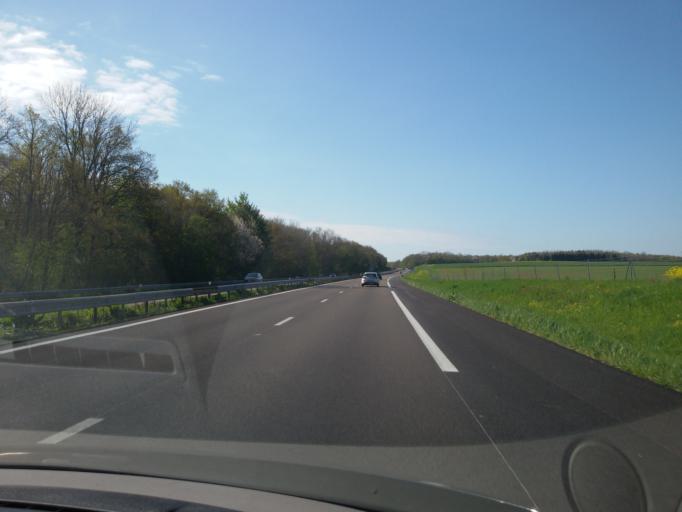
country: FR
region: Bourgogne
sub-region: Departement de l'Yonne
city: Joux-la-Ville
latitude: 47.6132
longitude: 3.9095
